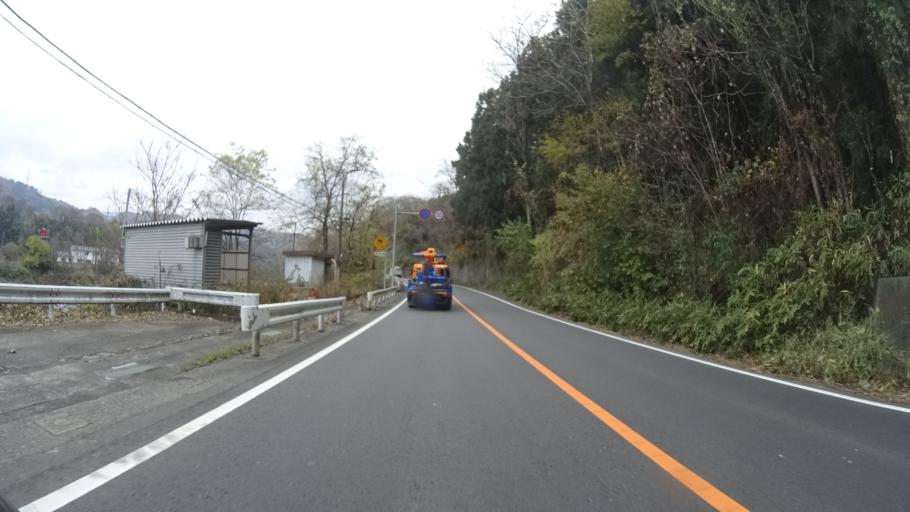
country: JP
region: Gunma
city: Numata
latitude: 36.6094
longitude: 139.0423
